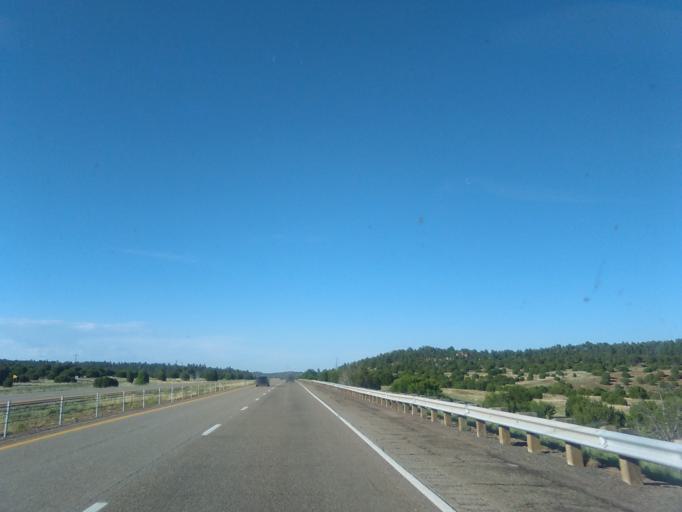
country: US
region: New Mexico
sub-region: San Miguel County
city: Las Vegas
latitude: 35.4999
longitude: -105.2640
